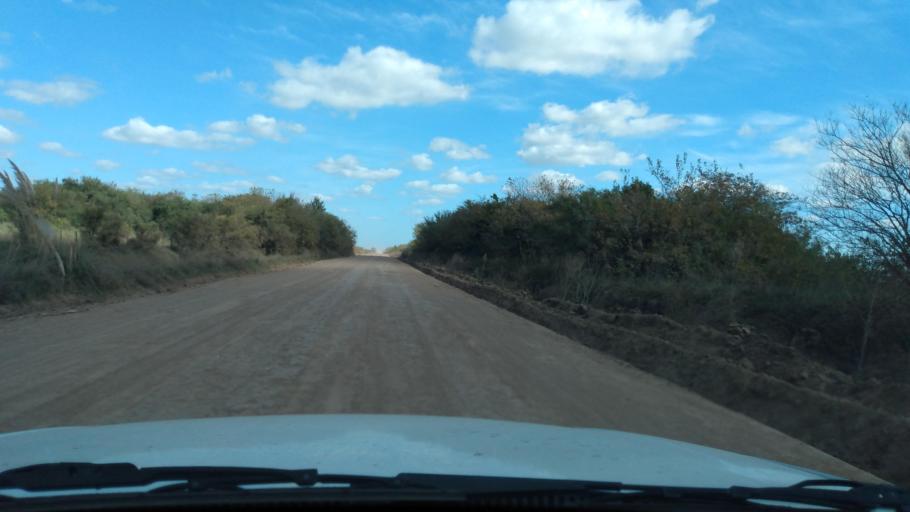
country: AR
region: Buenos Aires
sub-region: Partido de Navarro
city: Navarro
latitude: -35.0307
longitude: -59.4503
